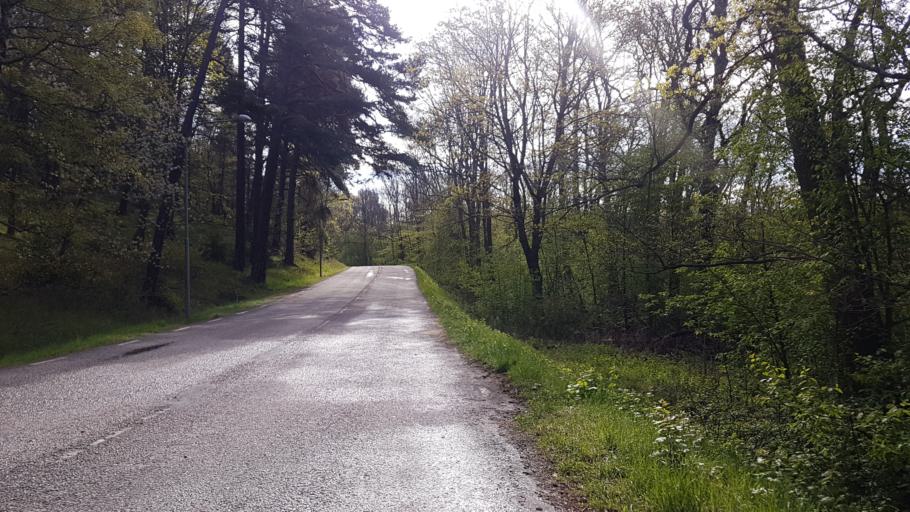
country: SE
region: Stockholm
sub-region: Stockholms Kommun
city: OEstermalm
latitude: 59.3560
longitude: 18.0697
